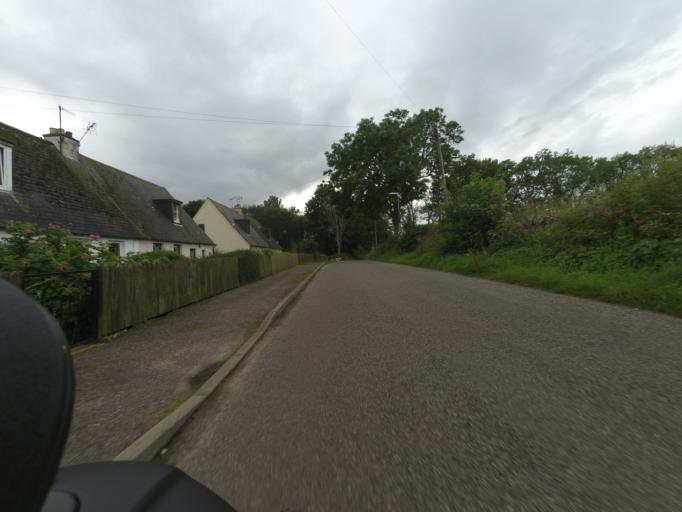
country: GB
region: Scotland
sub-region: Highland
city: Muir of Ord
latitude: 57.5124
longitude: -4.3887
